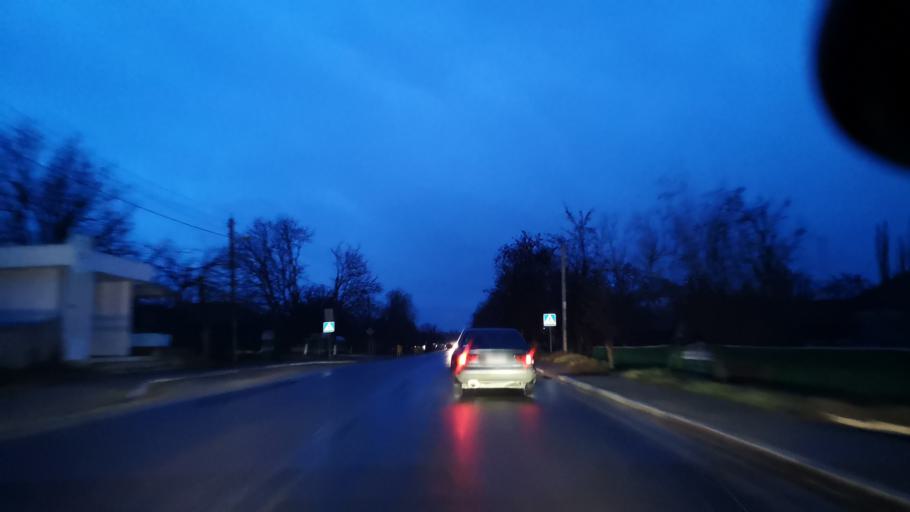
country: MD
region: Orhei
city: Orhei
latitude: 47.4242
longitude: 28.8049
